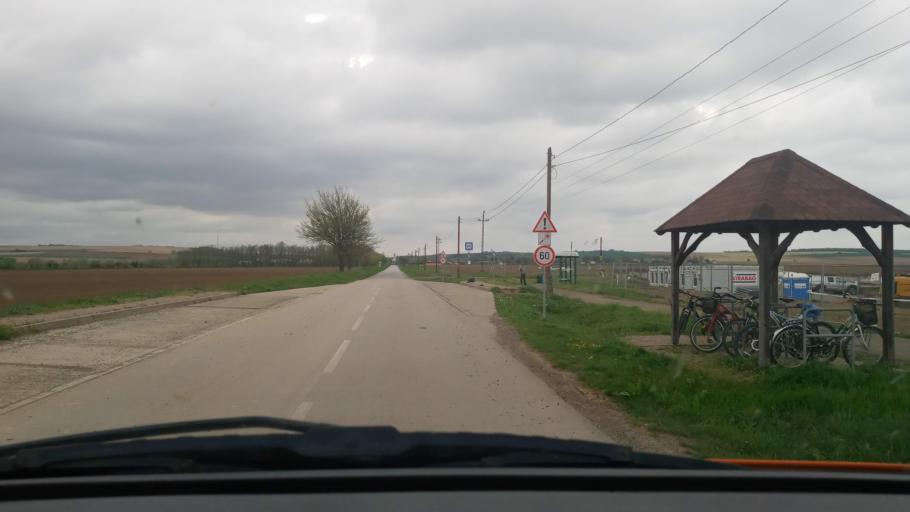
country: HU
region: Baranya
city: Boly
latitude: 45.9884
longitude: 18.5611
